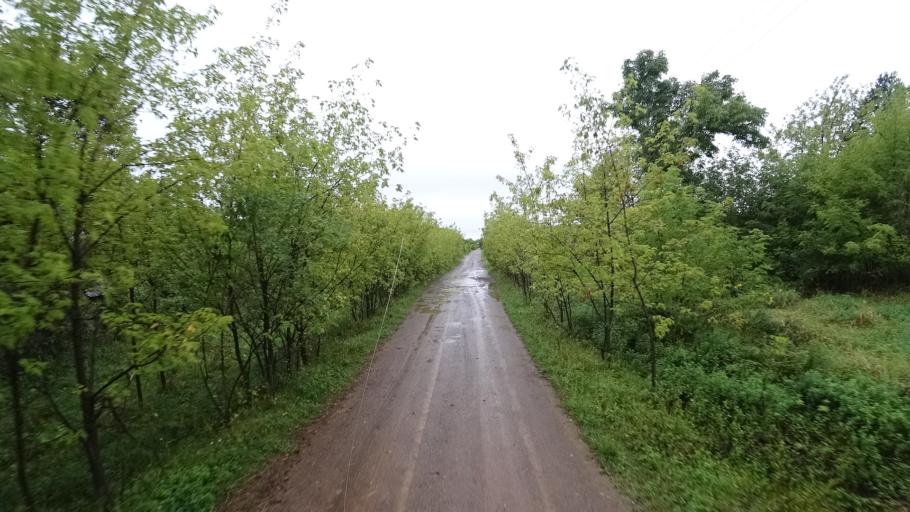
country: RU
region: Primorskiy
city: Monastyrishche
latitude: 44.2628
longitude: 132.4255
